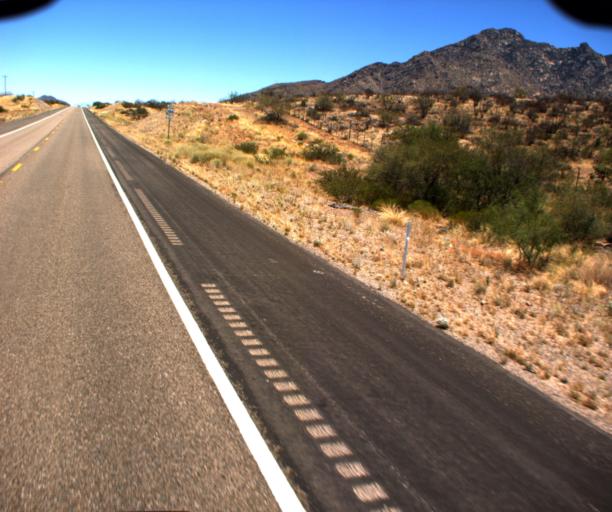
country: US
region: Arizona
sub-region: Pima County
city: Three Points
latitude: 32.0249
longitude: -111.5873
